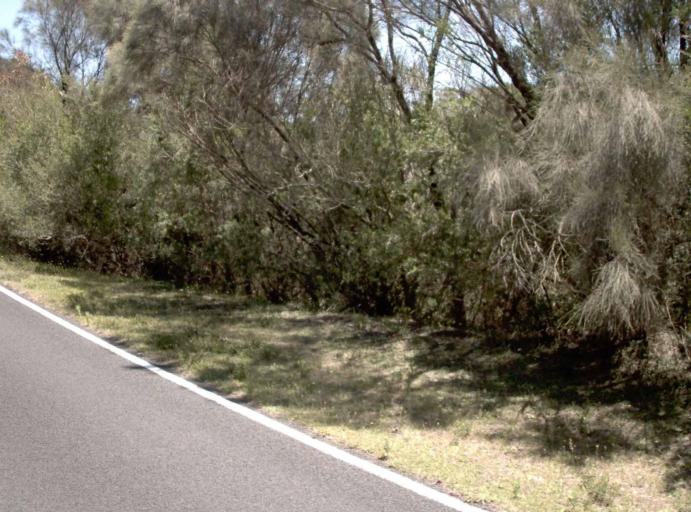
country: AU
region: Victoria
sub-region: Latrobe
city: Morwell
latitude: -38.8827
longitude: 146.2622
